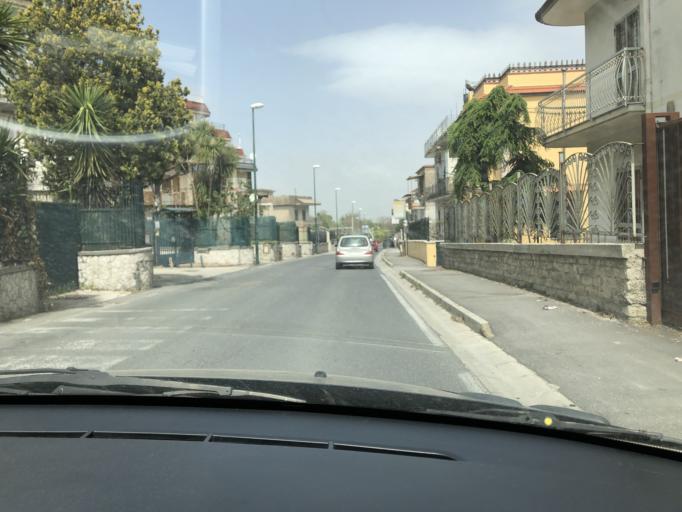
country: IT
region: Campania
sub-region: Provincia di Napoli
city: Torre Caracciolo
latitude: 40.8737
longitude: 14.1870
